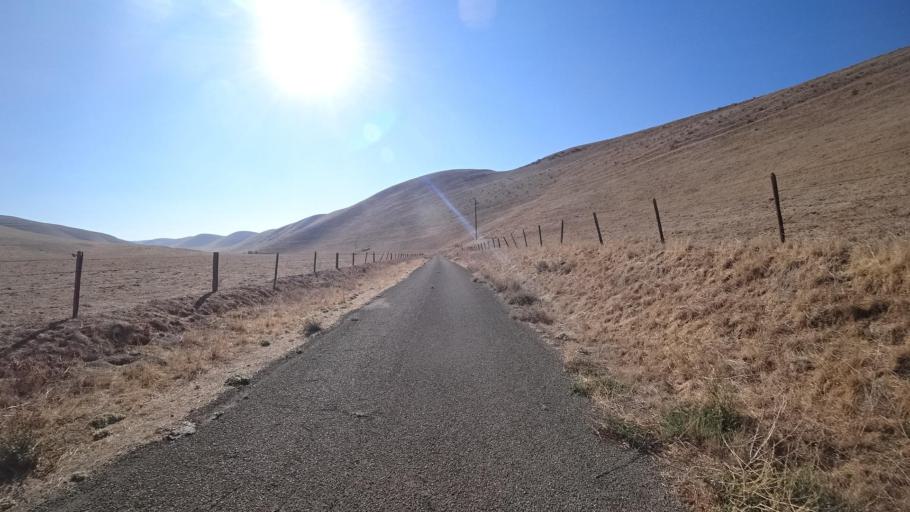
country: US
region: California
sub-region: Monterey County
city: King City
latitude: 36.1940
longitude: -121.0007
